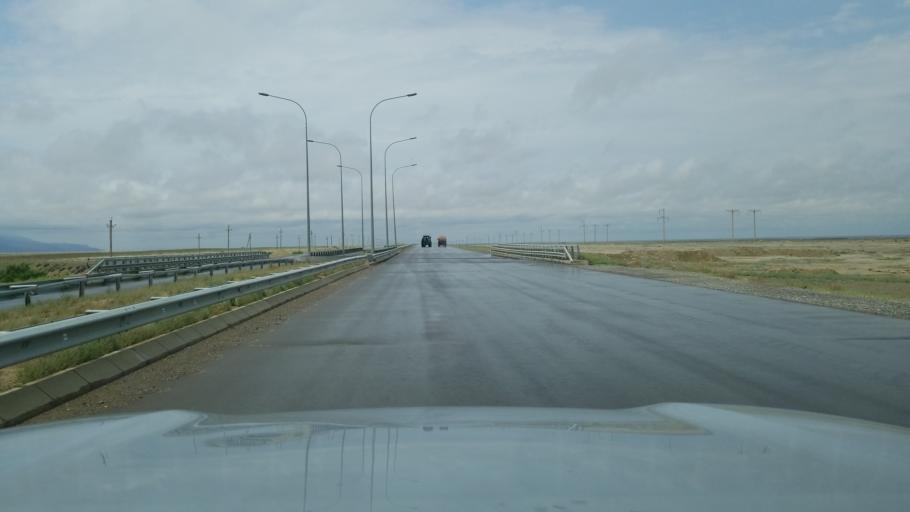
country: TM
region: Balkan
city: Gazanjyk
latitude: 39.1781
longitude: 55.8082
